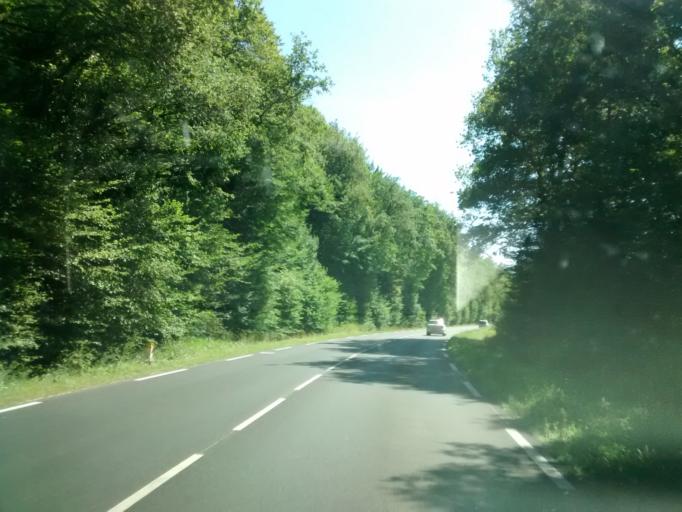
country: FR
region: Aquitaine
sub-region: Departement de la Dordogne
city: Bassillac
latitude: 45.1151
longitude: 0.8328
